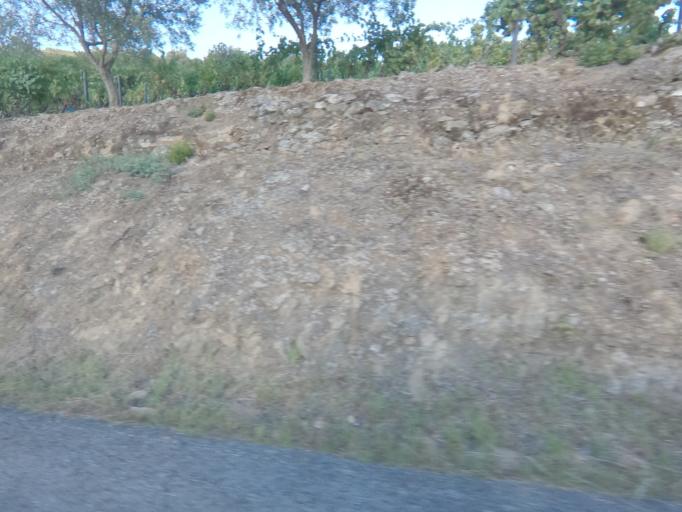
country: PT
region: Viseu
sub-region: Armamar
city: Armamar
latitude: 41.1650
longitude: -7.6839
